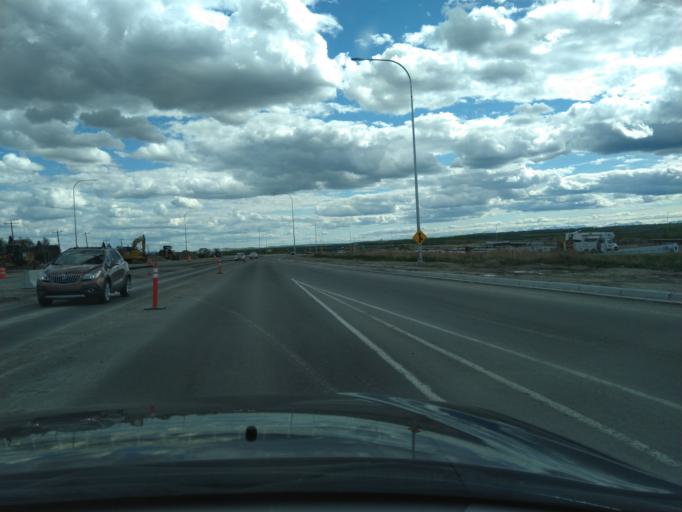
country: CA
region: Alberta
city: Calgary
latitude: 51.0069
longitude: -114.1419
